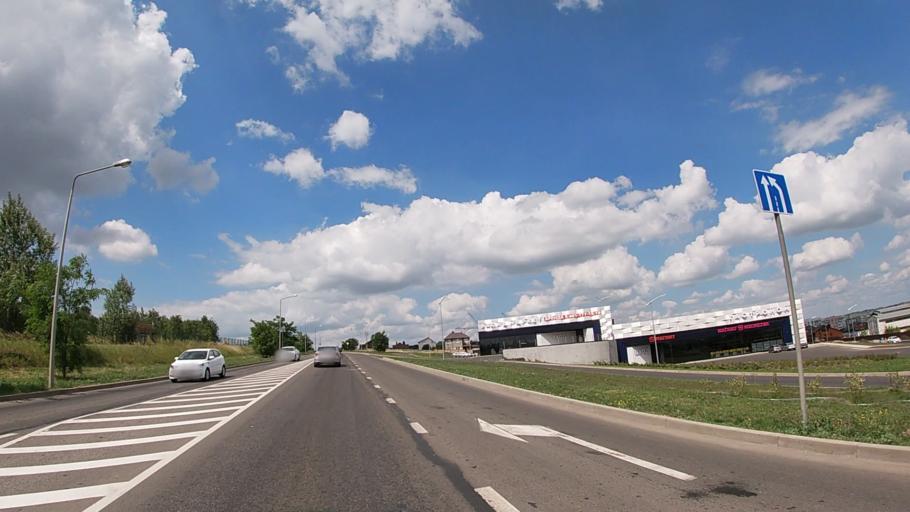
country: RU
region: Belgorod
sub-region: Belgorodskiy Rayon
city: Belgorod
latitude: 50.5949
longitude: 36.5409
